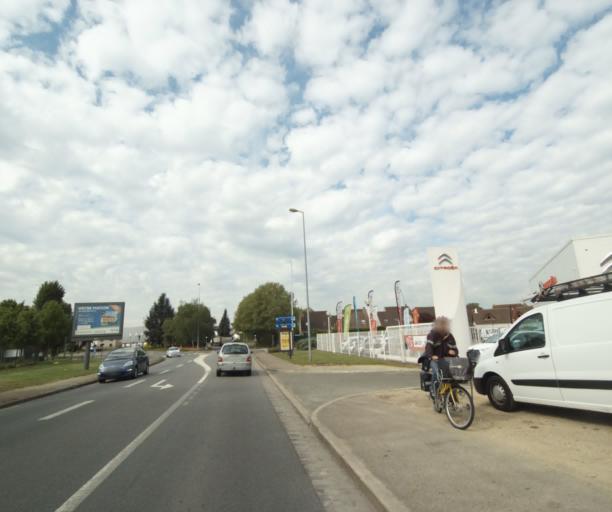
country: FR
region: Ile-de-France
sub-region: Departement des Yvelines
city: Les Mureaux
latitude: 48.9980
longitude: 1.9145
